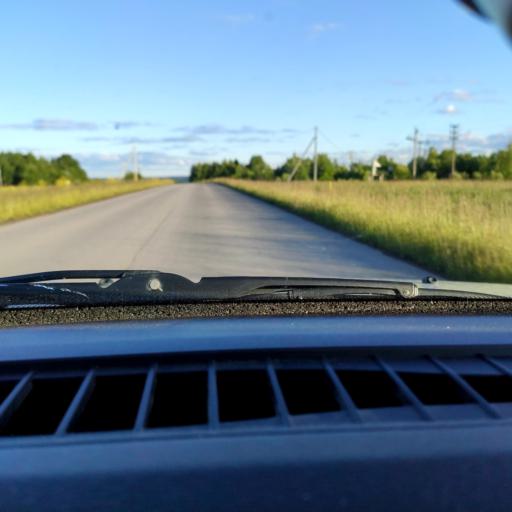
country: RU
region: Perm
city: Novyye Lyady
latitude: 58.1897
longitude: 56.5398
